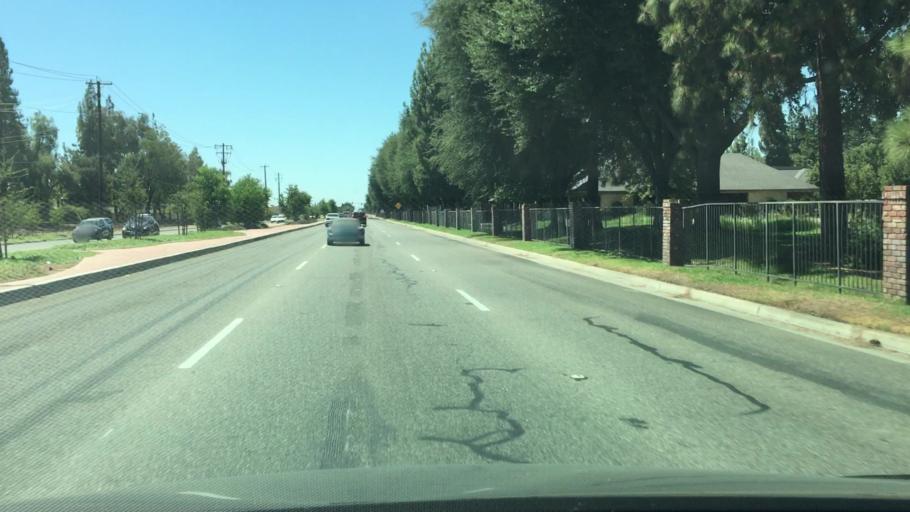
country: US
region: California
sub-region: Fresno County
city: Fresno
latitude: 36.8373
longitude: -119.8566
